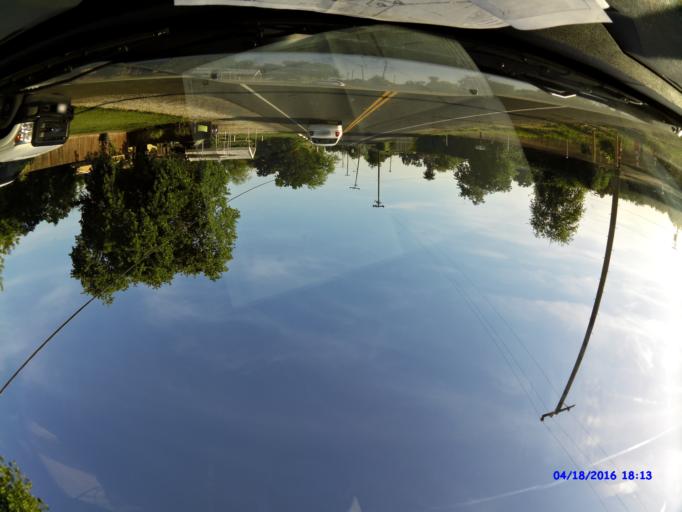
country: US
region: California
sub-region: San Joaquin County
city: Linden
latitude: 37.9281
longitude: -121.0002
